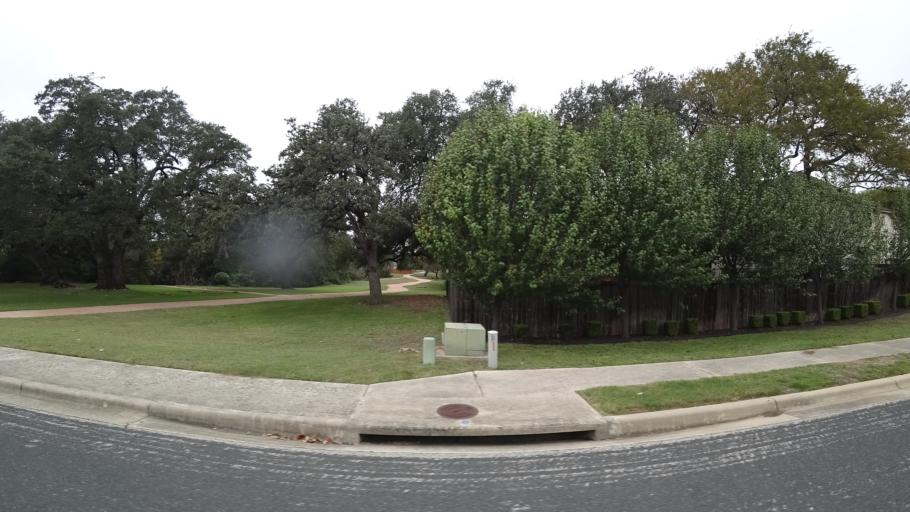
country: US
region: Texas
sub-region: Williamson County
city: Anderson Mill
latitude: 30.4477
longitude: -97.8203
